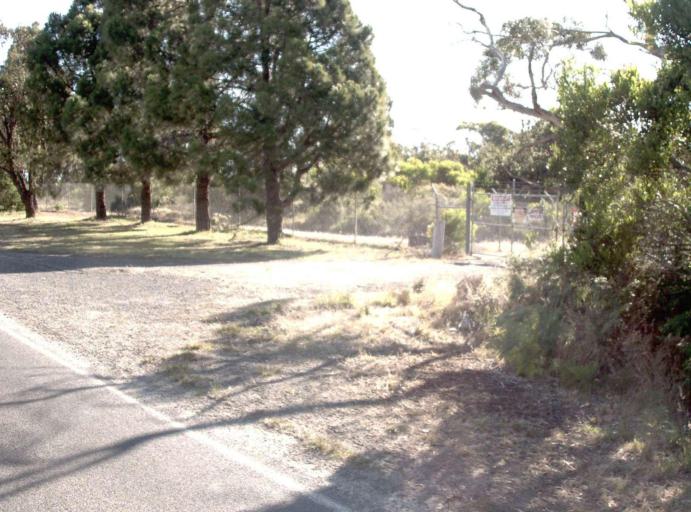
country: AU
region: Victoria
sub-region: Latrobe
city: Morwell
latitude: -38.7075
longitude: 146.3973
